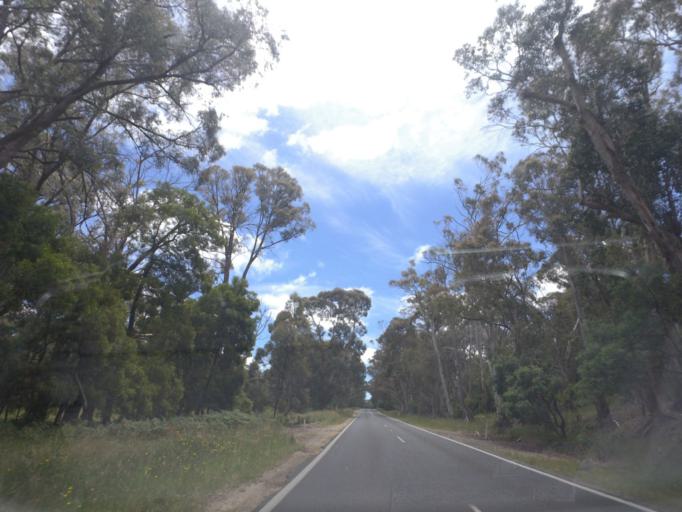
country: AU
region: Victoria
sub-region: Mount Alexander
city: Castlemaine
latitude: -37.3291
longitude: 144.1660
